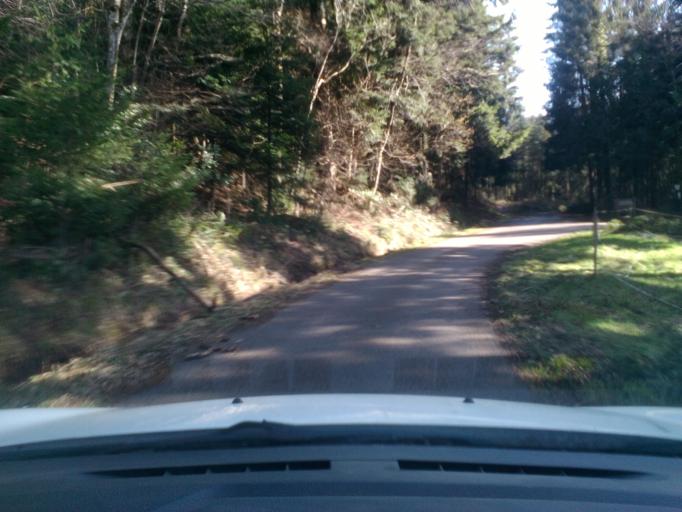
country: FR
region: Lorraine
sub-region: Departement des Vosges
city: Saint-Die-des-Vosges
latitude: 48.3185
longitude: 6.9859
